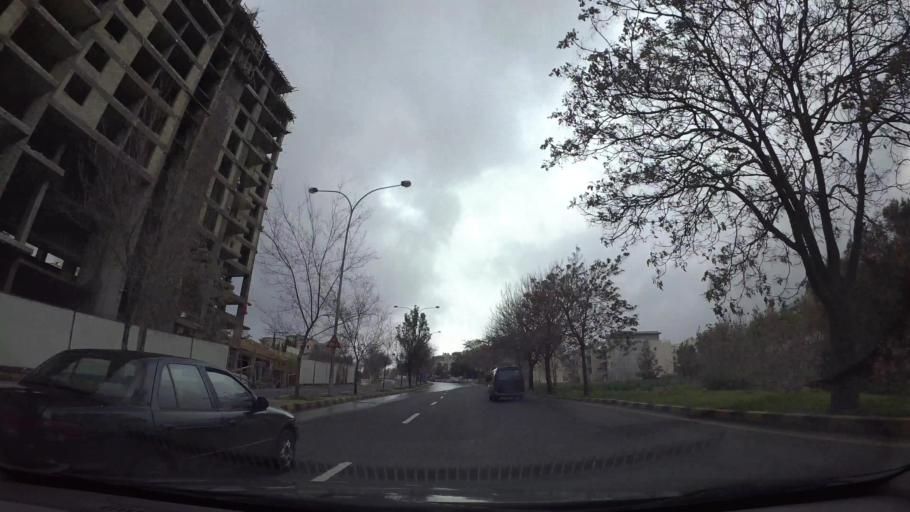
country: JO
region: Amman
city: Al Bunayyat ash Shamaliyah
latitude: 31.9464
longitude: 35.8866
